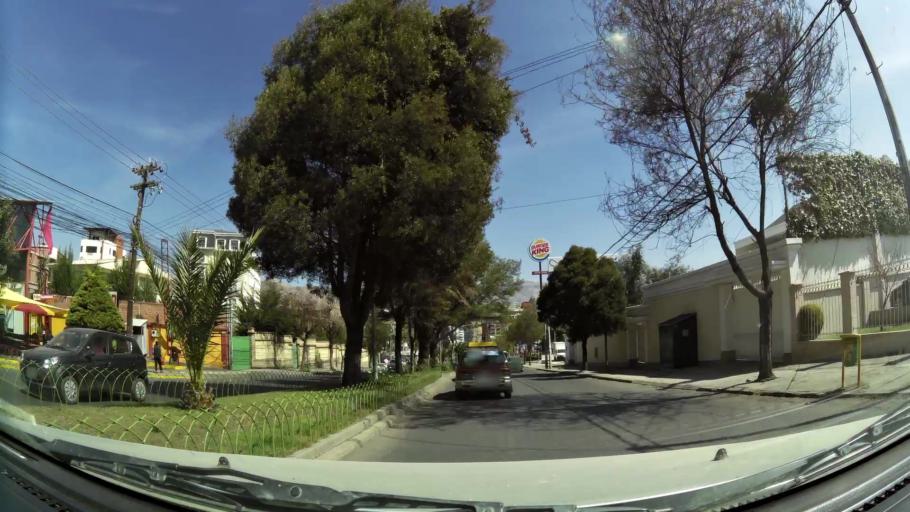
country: BO
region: La Paz
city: La Paz
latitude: -16.5389
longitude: -68.0791
